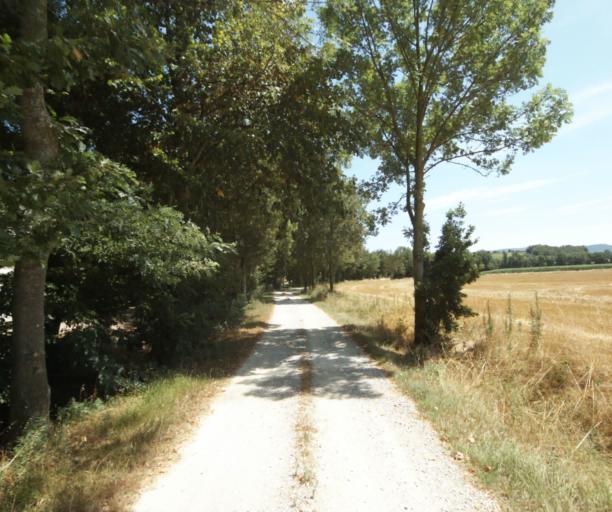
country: FR
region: Midi-Pyrenees
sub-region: Departement de la Haute-Garonne
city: Revel
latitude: 43.5012
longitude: 2.0396
